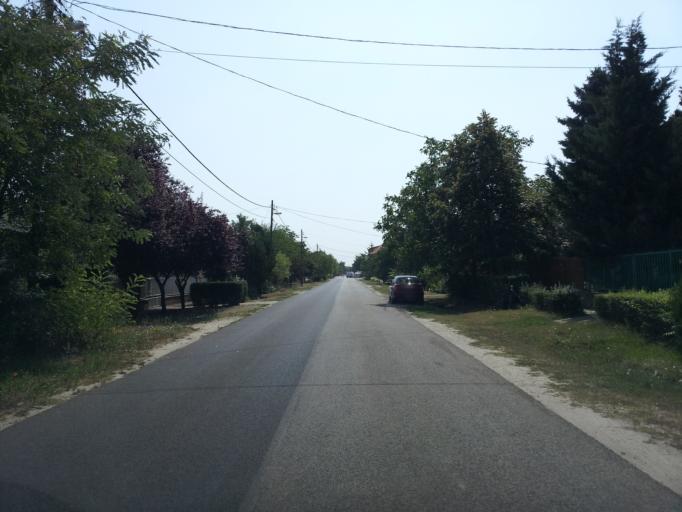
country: HU
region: Pest
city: Dunavarsany
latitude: 47.2809
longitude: 19.0691
